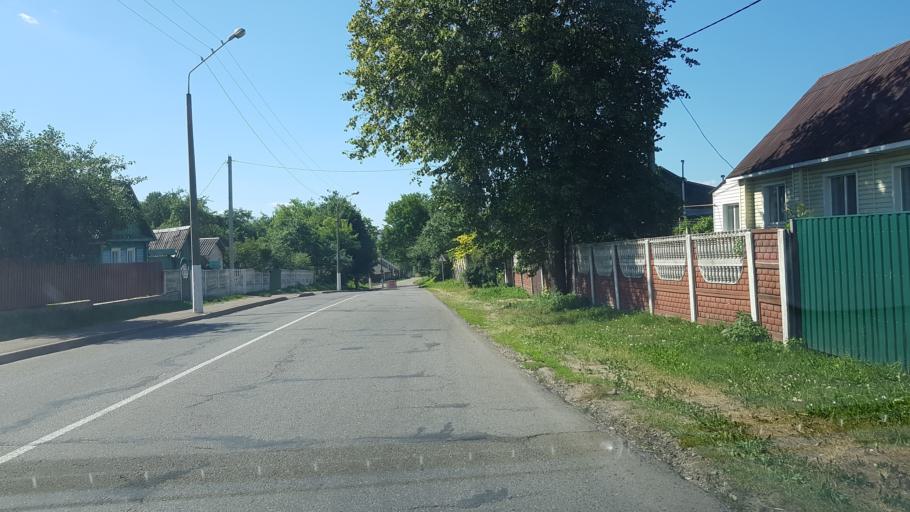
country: BY
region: Vitebsk
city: Orsha
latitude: 54.5048
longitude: 30.4356
